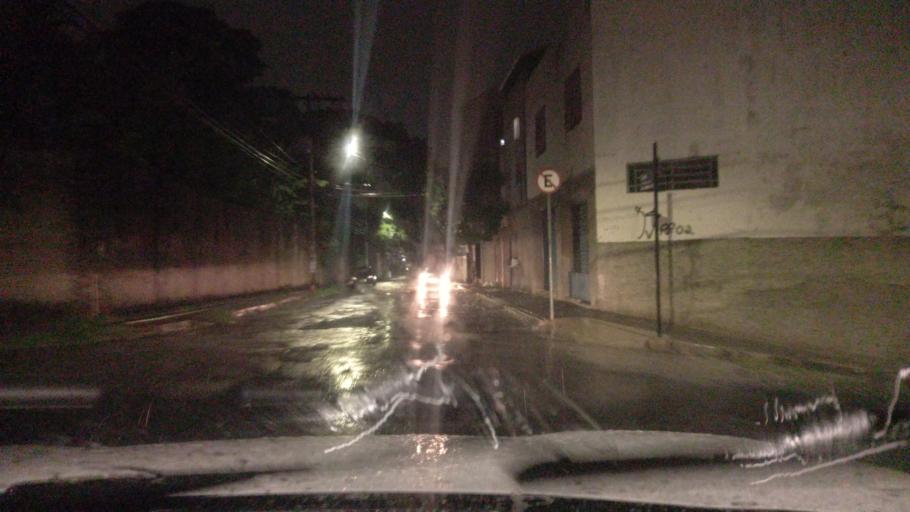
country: BR
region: Minas Gerais
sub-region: Belo Horizonte
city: Belo Horizonte
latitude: -19.9105
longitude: -43.9786
